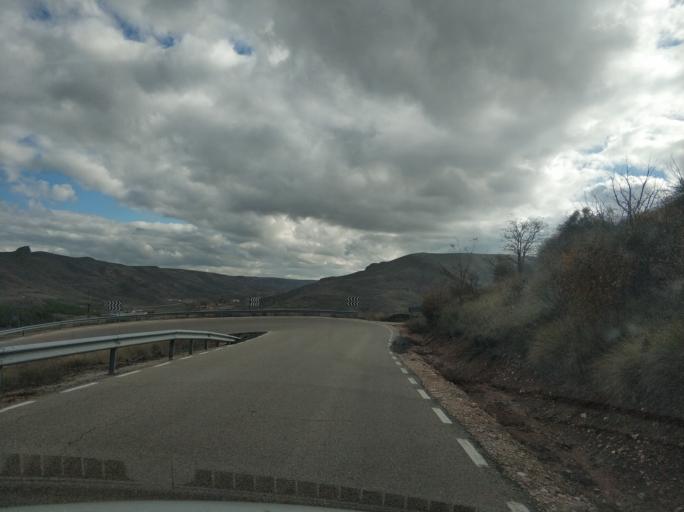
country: ES
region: Castille and Leon
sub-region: Provincia de Soria
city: Medinaceli
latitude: 41.1630
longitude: -2.4259
